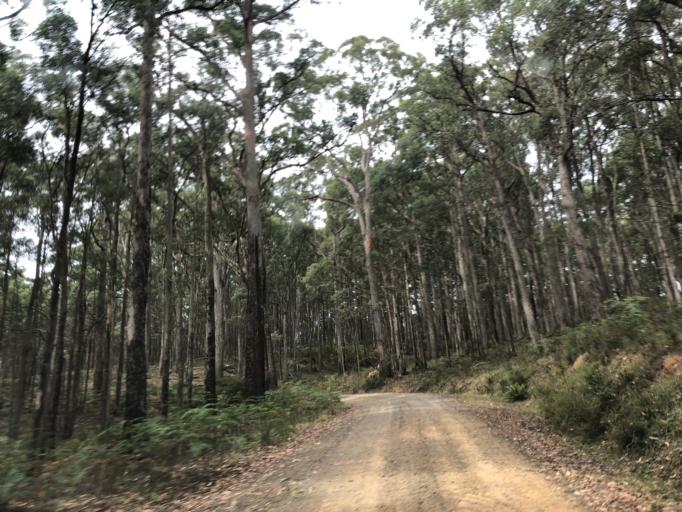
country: AU
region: Victoria
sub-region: Moorabool
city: Bacchus Marsh
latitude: -37.4404
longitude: 144.3437
